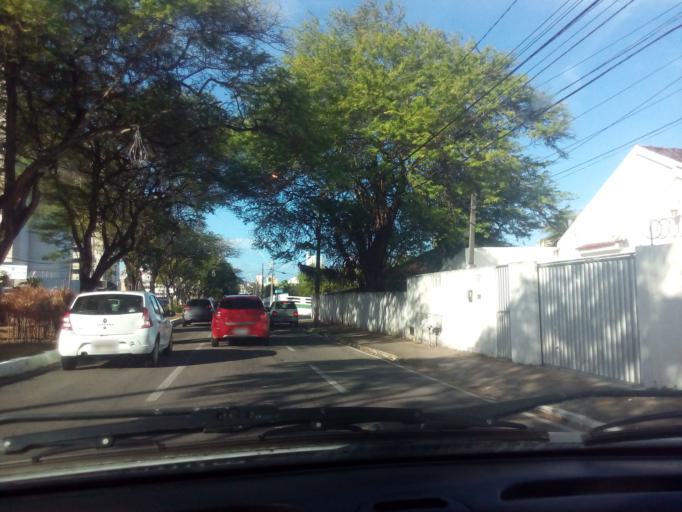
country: BR
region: Rio Grande do Norte
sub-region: Natal
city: Natal
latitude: -5.8058
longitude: -35.2025
